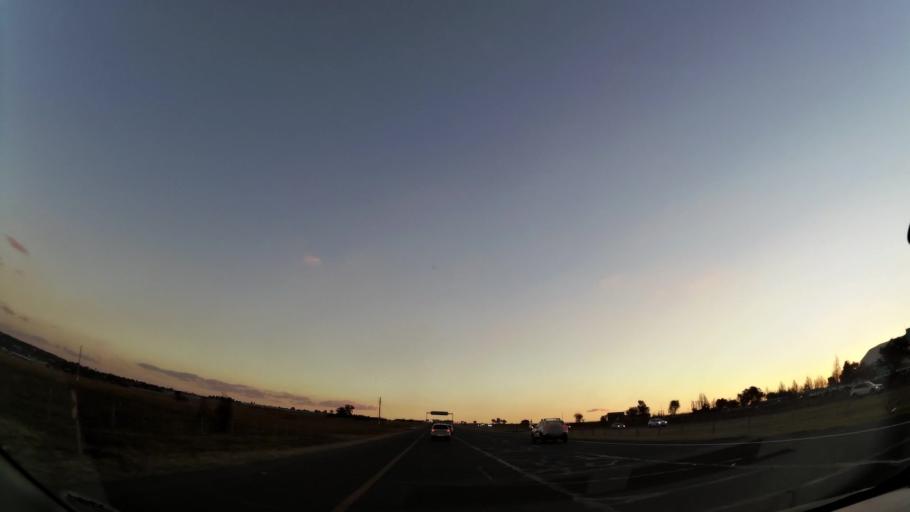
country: ZA
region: Mpumalanga
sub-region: Nkangala District Municipality
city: Witbank
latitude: -25.8896
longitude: 29.2686
